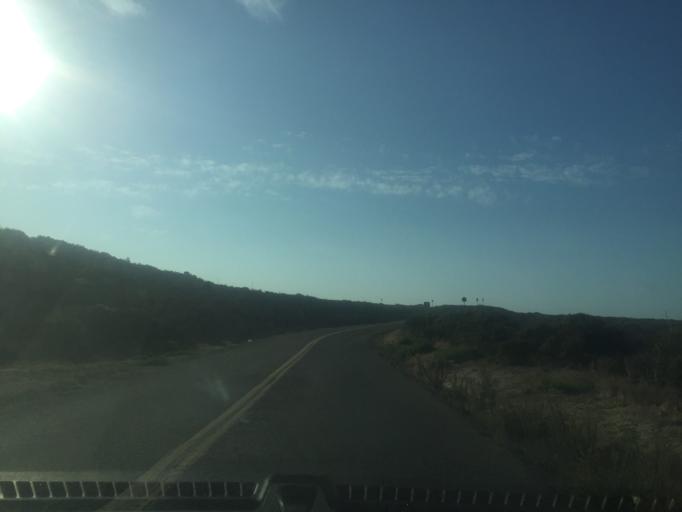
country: US
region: California
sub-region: Santa Barbara County
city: Lompoc
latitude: 34.5033
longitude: -120.4978
